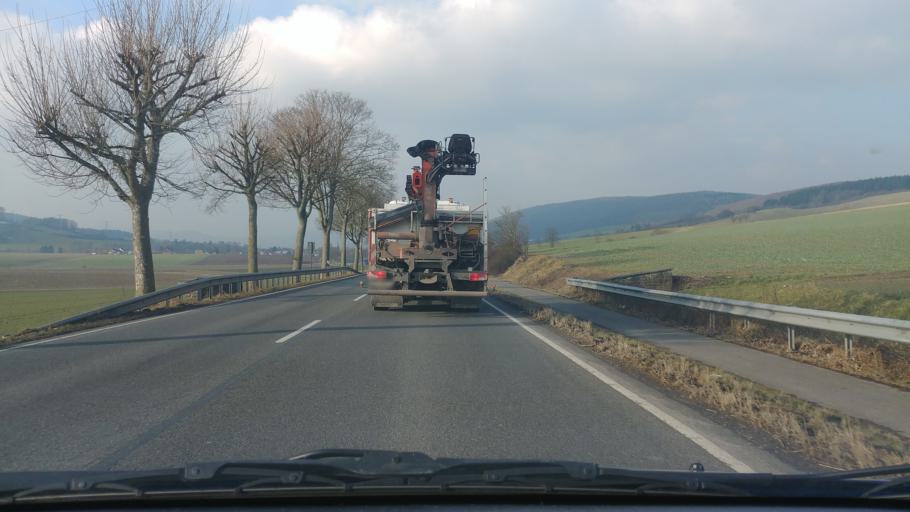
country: DE
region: Lower Saxony
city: Freden
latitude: 51.8983
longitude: 9.8698
